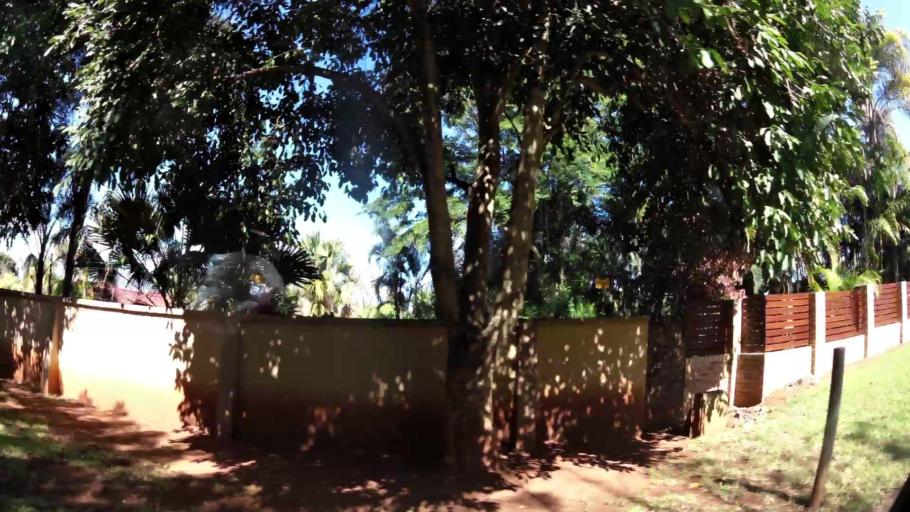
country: ZA
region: Limpopo
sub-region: Mopani District Municipality
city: Tzaneen
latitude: -23.8123
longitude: 30.1512
